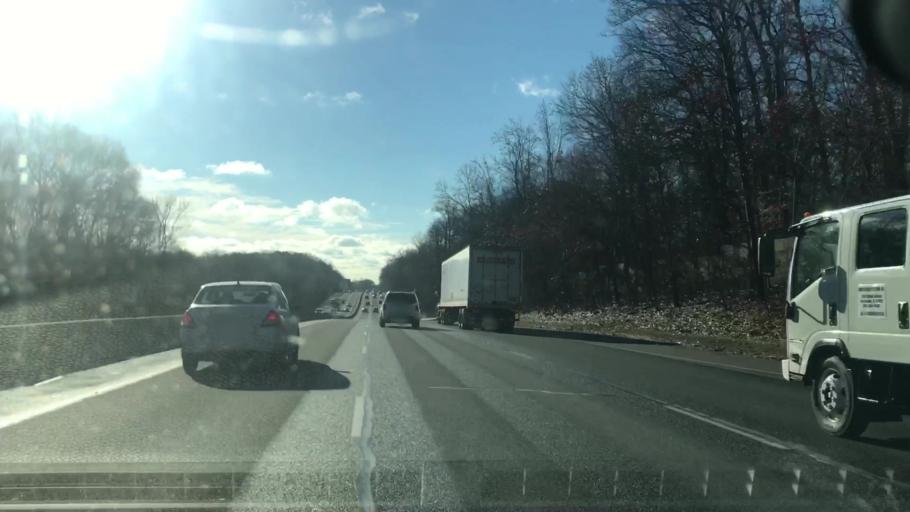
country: US
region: New Jersey
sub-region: Bergen County
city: Saddle River
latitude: 41.0289
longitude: -74.1106
